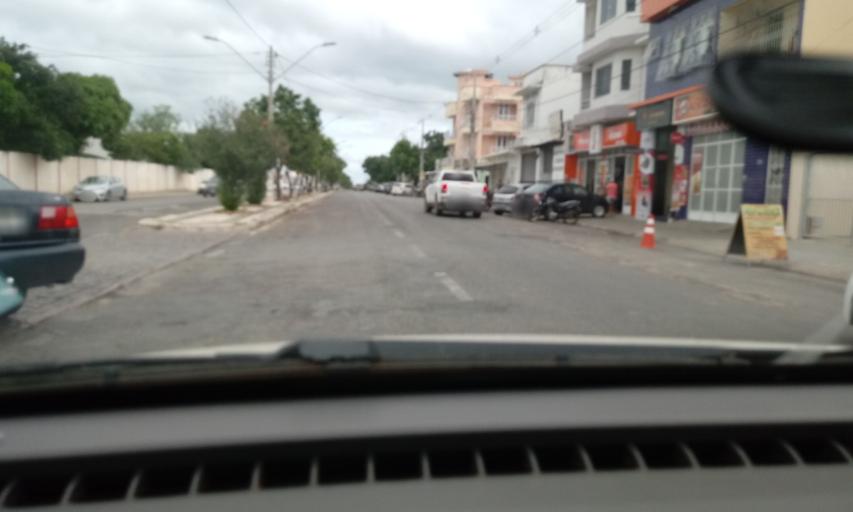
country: BR
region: Bahia
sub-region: Guanambi
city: Guanambi
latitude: -14.2164
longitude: -42.7838
